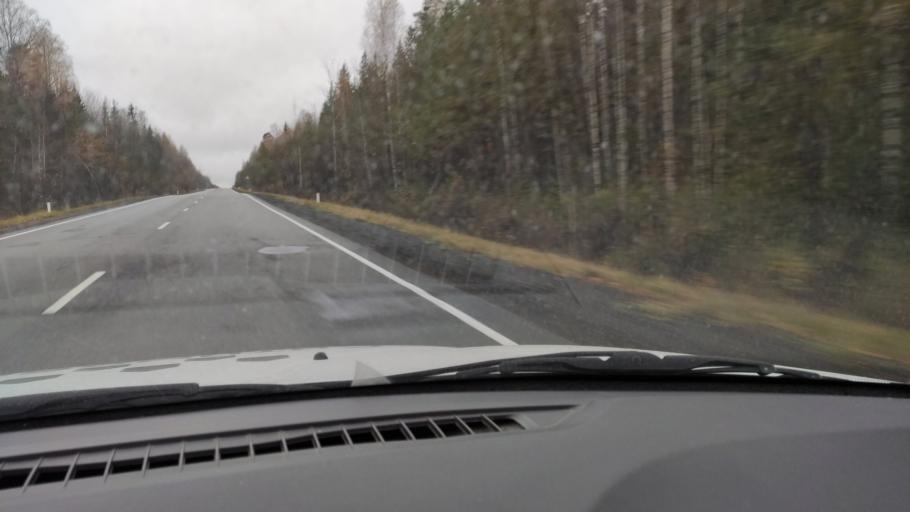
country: RU
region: Kirov
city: Chernaya Kholunitsa
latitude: 58.8684
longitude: 51.5593
